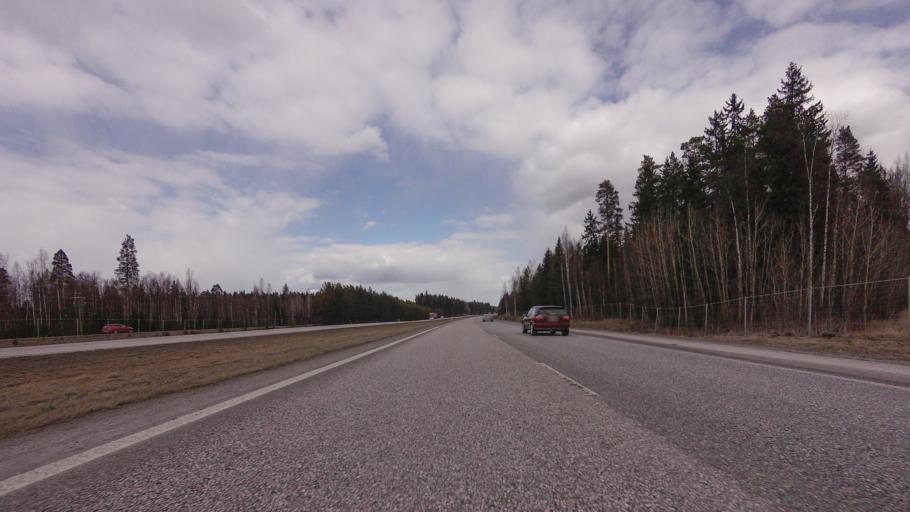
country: FI
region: Uusimaa
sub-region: Helsinki
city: Nurmijaervi
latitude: 60.4259
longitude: 24.8264
